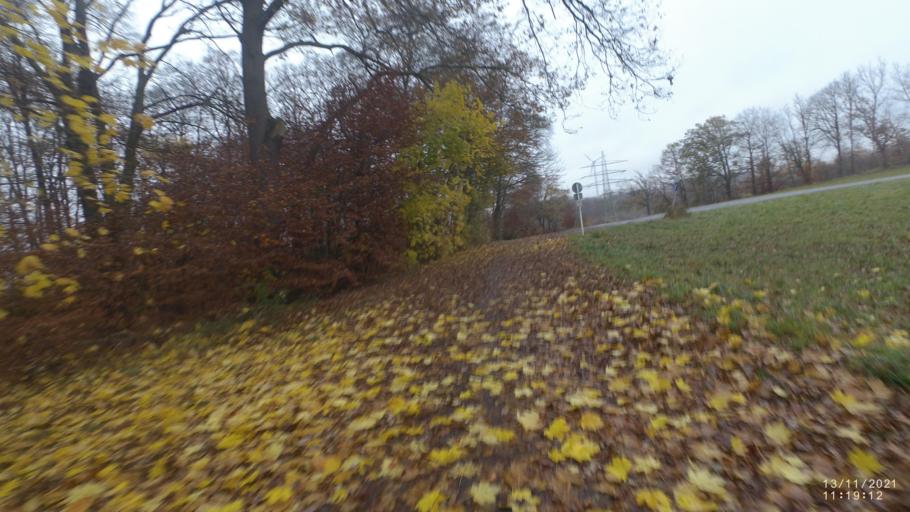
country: DE
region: North Rhine-Westphalia
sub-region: Regierungsbezirk Arnsberg
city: Luedenscheid
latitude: 51.2342
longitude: 7.6435
